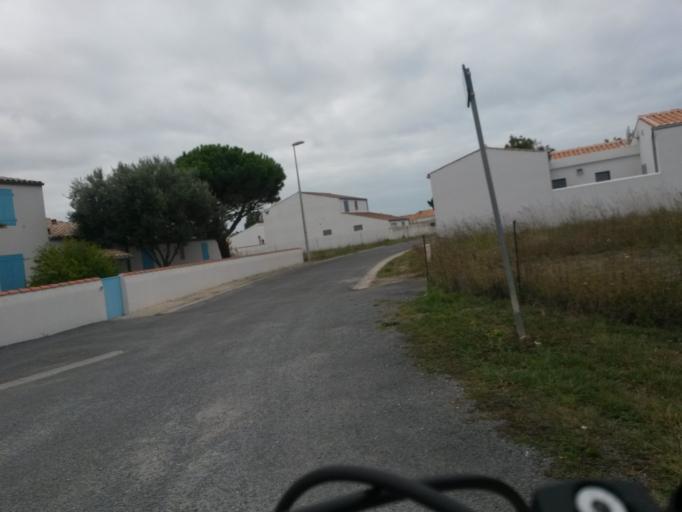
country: FR
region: Poitou-Charentes
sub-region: Departement de la Charente-Maritime
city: Saint-Denis-d'Oleron
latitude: 46.0389
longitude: -1.3804
